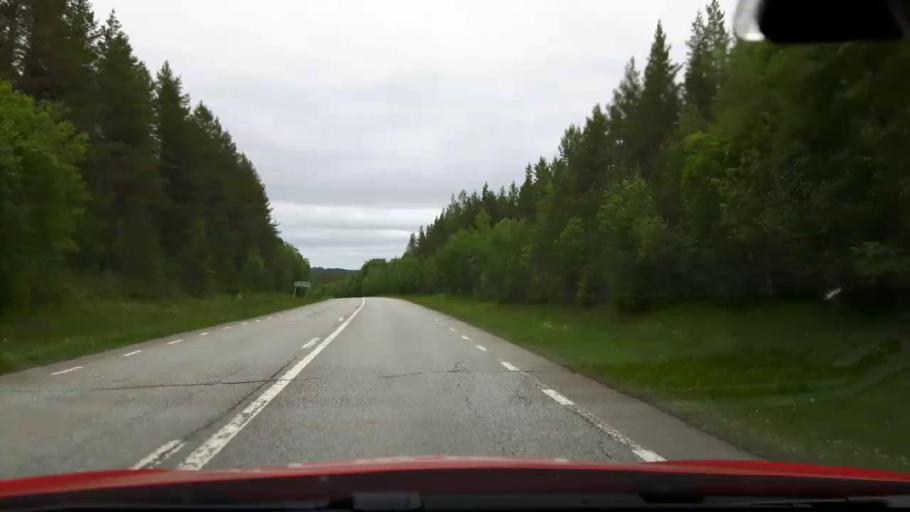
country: SE
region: Jaemtland
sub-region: OEstersunds Kommun
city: Lit
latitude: 63.6076
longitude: 14.6722
